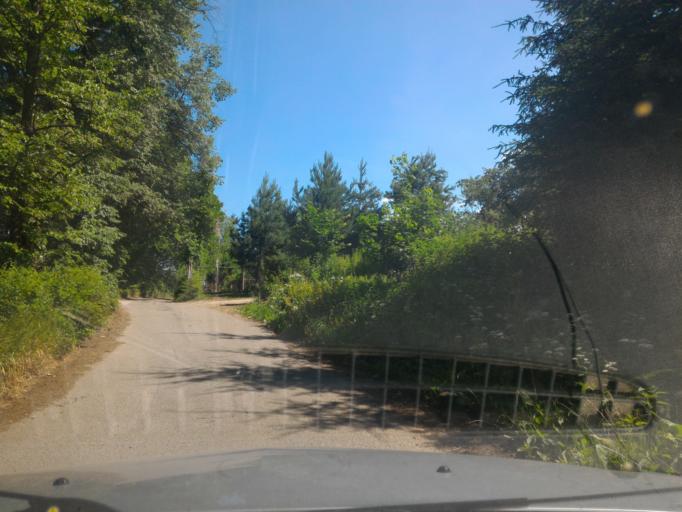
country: CZ
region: Vysocina
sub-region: Okres Jihlava
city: Telc
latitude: 49.1791
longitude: 15.4641
